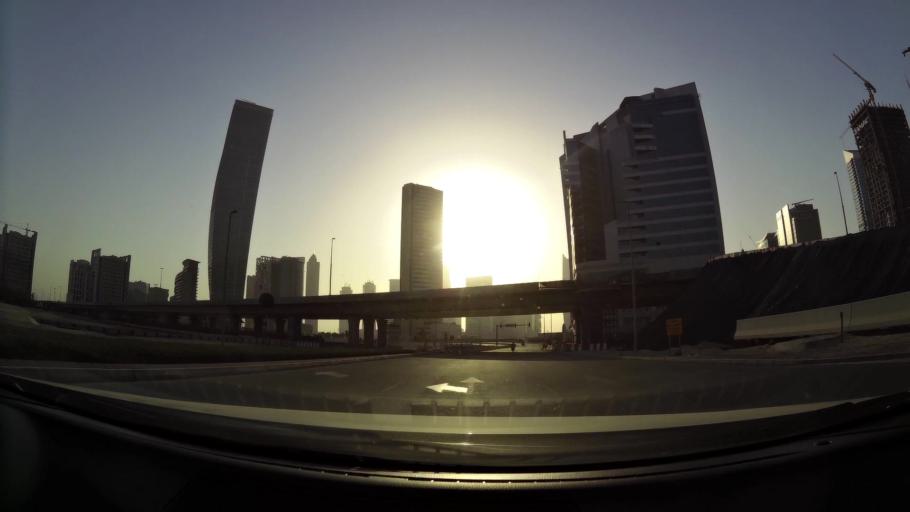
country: AE
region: Dubai
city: Dubai
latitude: 25.1819
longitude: 55.2758
